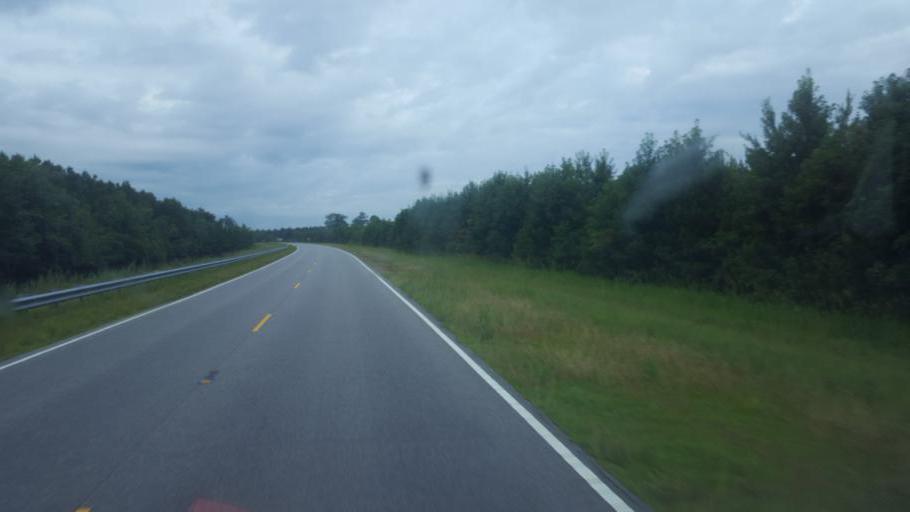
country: US
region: North Carolina
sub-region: Tyrrell County
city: Columbia
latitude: 35.9340
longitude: -76.1570
